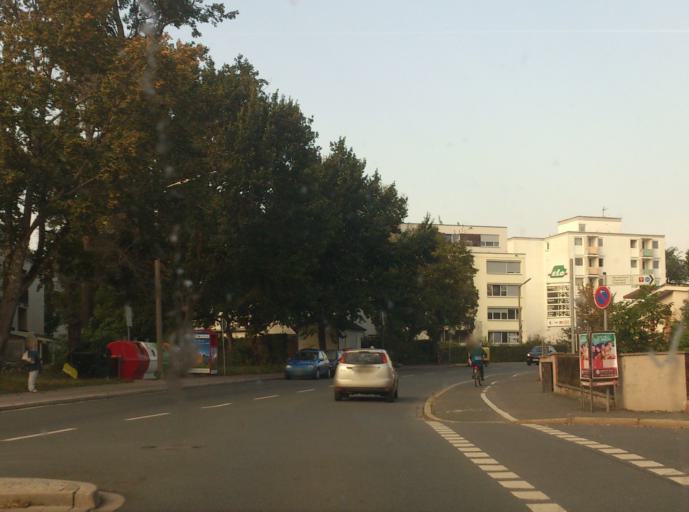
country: DE
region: Bavaria
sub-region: Regierungsbezirk Mittelfranken
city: Buckenhof
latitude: 49.5993
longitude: 11.0376
